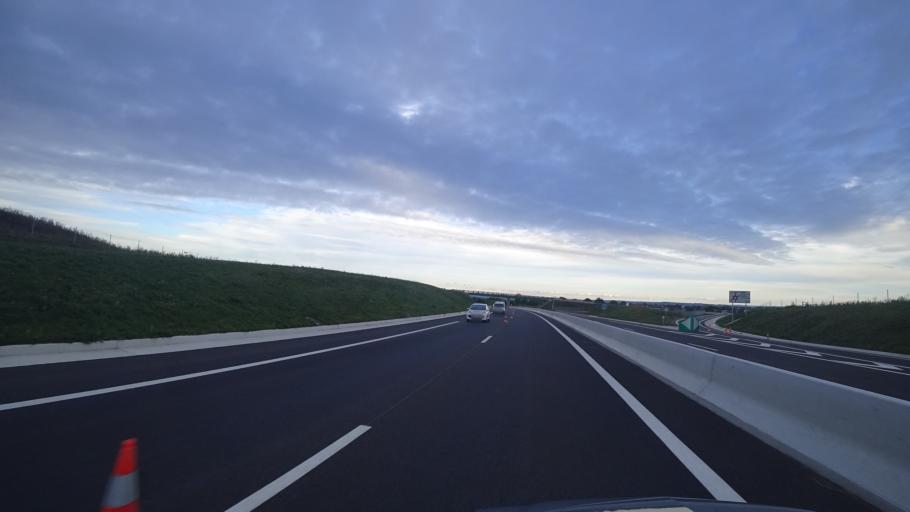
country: FR
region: Midi-Pyrenees
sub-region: Departement de l'Aveyron
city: Luc-la-Primaube
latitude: 44.2906
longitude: 2.5078
